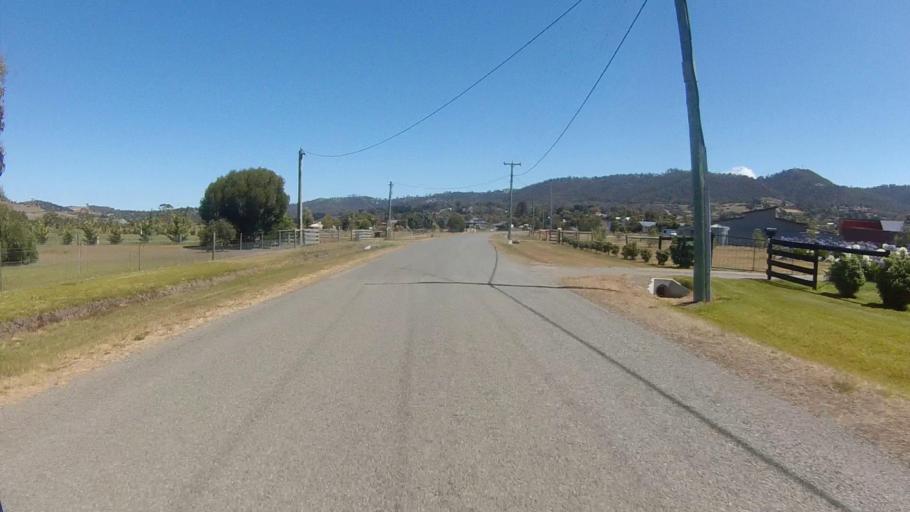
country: AU
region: Tasmania
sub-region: Clarence
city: Seven Mile Beach
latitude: -42.8517
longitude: 147.4913
